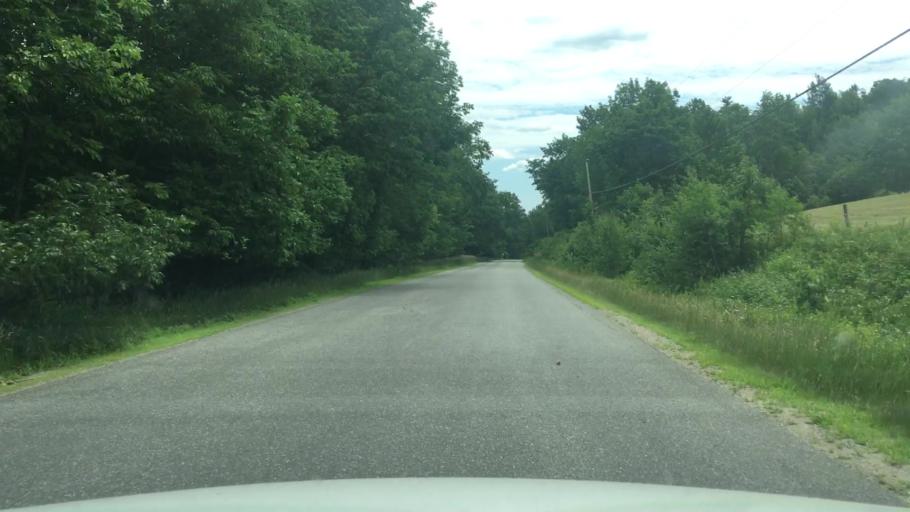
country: US
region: Maine
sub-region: Waldo County
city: Searsmont
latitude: 44.4509
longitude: -69.2509
